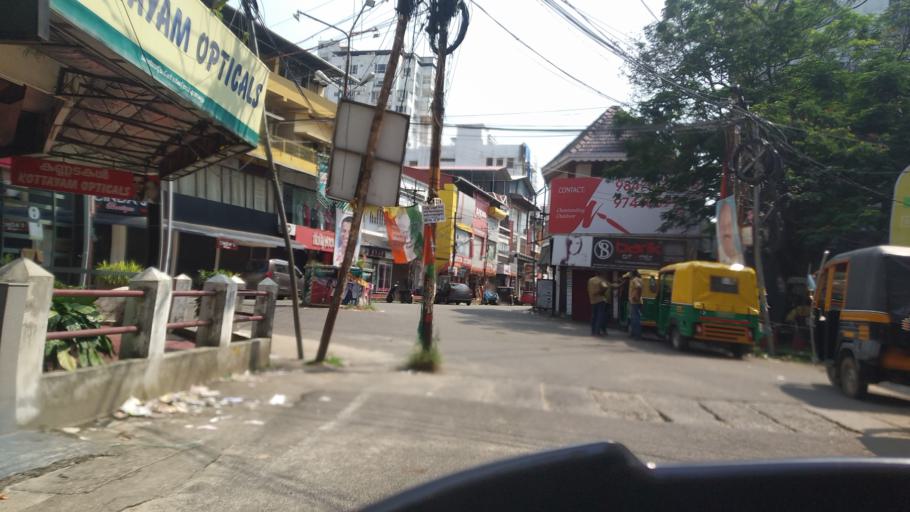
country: IN
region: Kerala
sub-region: Ernakulam
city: Cochin
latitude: 9.9765
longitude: 76.2802
